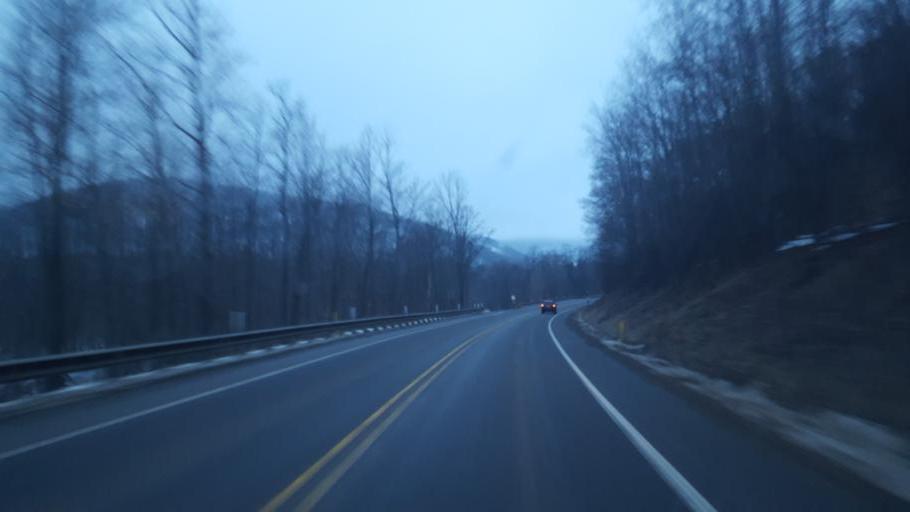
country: US
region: Pennsylvania
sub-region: Potter County
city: Coudersport
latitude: 41.7517
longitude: -78.1022
